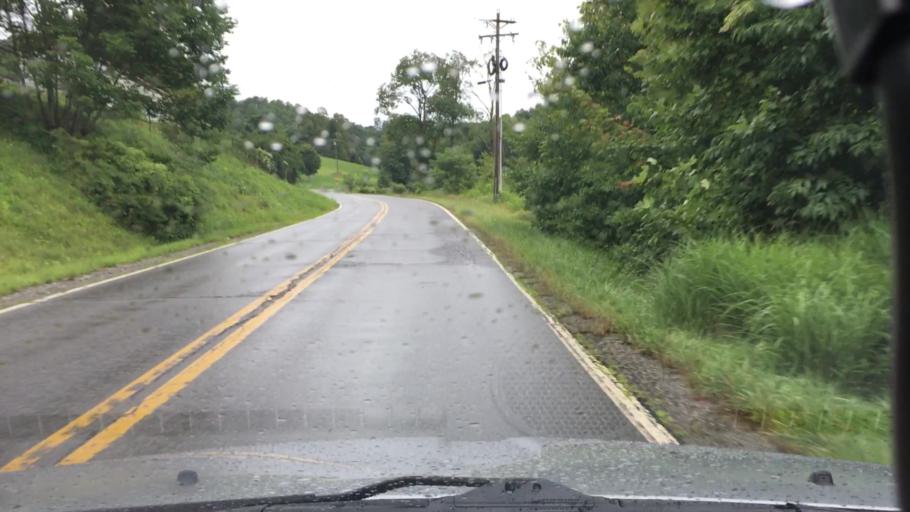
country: US
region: North Carolina
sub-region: Madison County
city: Mars Hill
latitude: 35.9322
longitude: -82.5331
